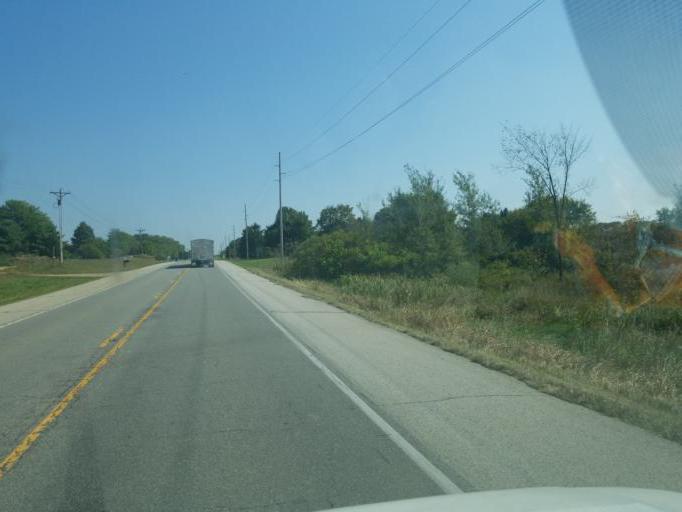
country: US
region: Indiana
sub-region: LaGrange County
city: Lagrange
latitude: 41.6420
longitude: -85.2099
